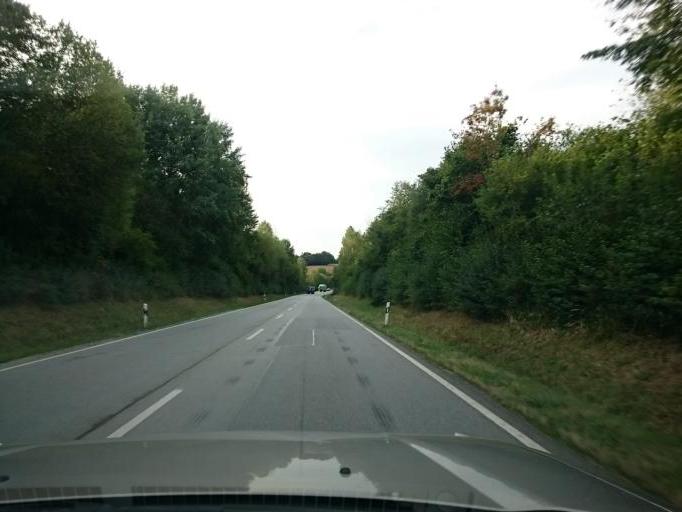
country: DE
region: Bavaria
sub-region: Lower Bavaria
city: Simbach
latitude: 48.5635
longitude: 12.7308
